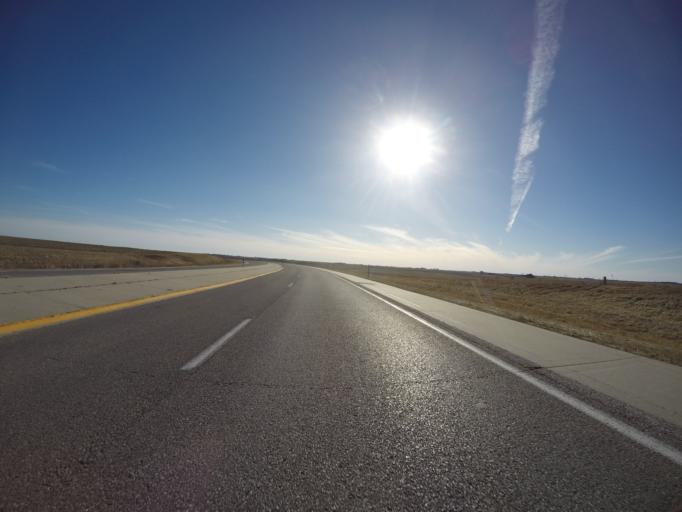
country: US
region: Nebraska
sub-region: Gage County
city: Beatrice
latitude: 40.4615
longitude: -96.7411
